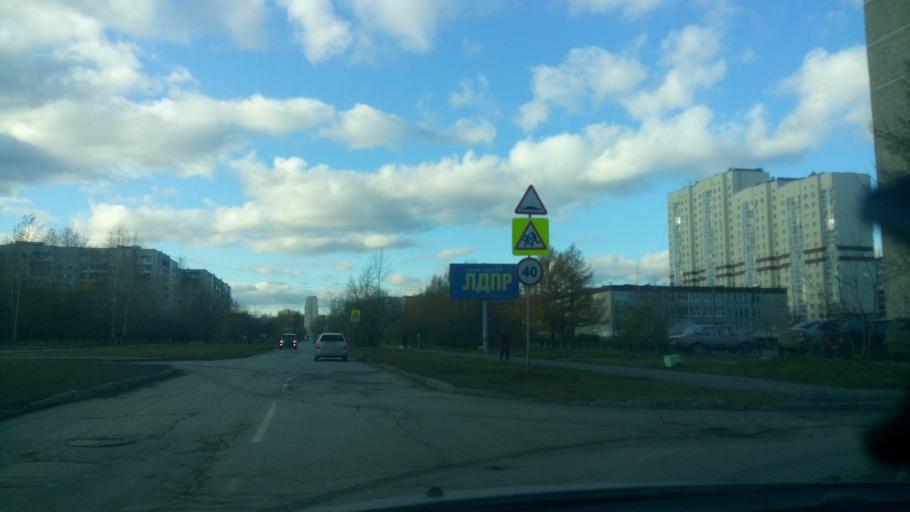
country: RU
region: Sverdlovsk
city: Yekaterinburg
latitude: 56.8655
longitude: 60.5421
